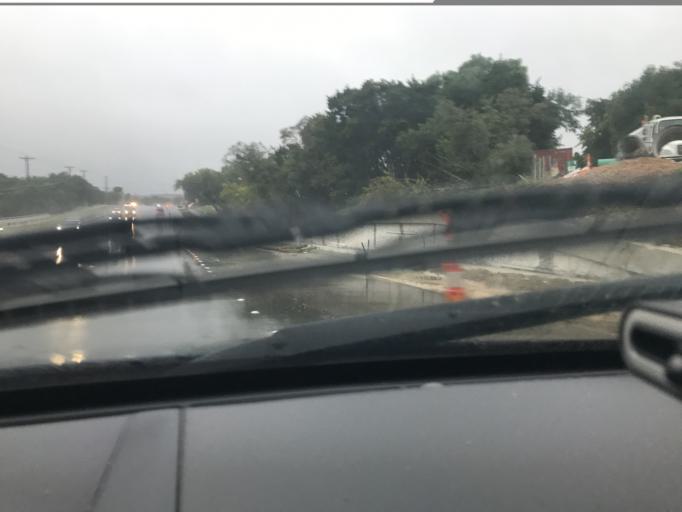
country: US
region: Texas
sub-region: Travis County
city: West Lake Hills
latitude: 30.2882
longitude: -97.8162
